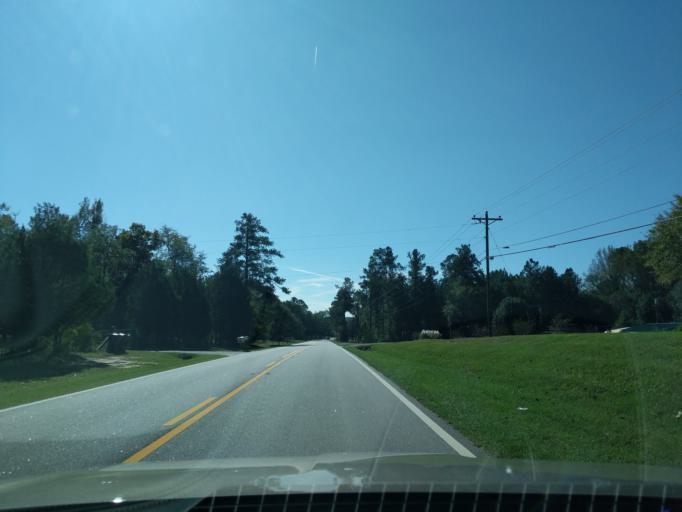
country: US
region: Georgia
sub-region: Richmond County
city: Hephzibah
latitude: 33.3116
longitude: -82.0186
